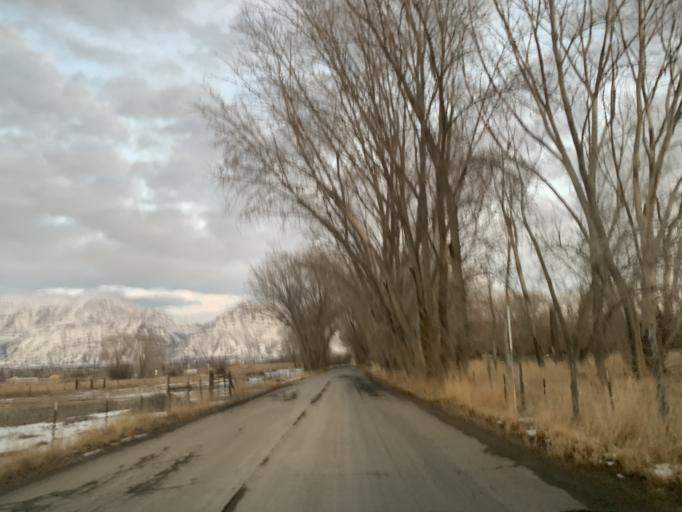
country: US
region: Utah
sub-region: Utah County
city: Orem
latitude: 40.2385
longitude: -111.7246
